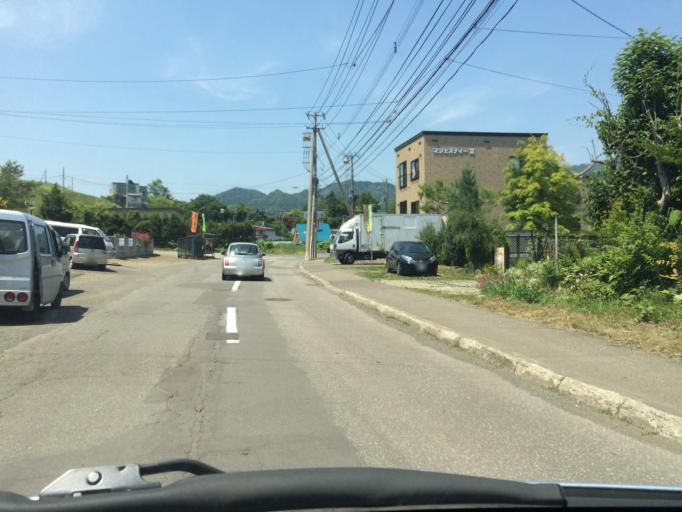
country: JP
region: Hokkaido
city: Sapporo
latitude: 42.9622
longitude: 141.2853
